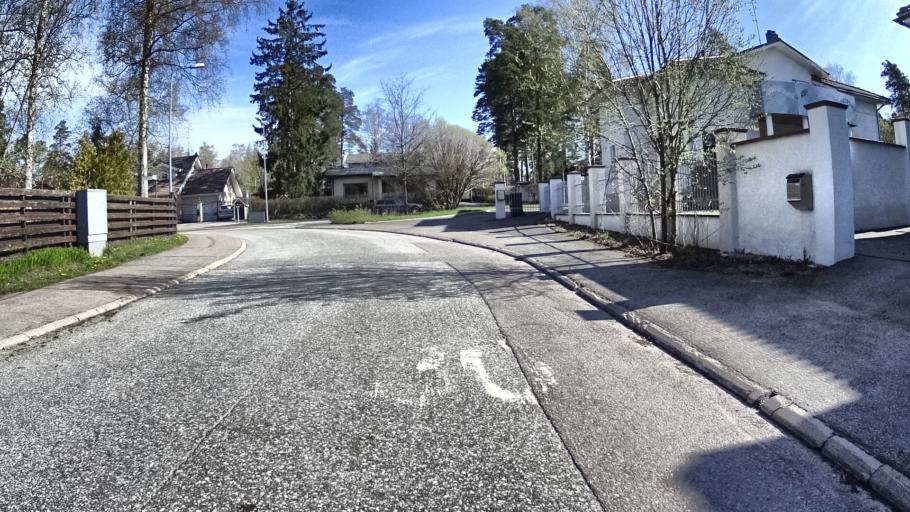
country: FI
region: Uusimaa
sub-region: Helsinki
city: Vantaa
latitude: 60.2262
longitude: 25.0584
